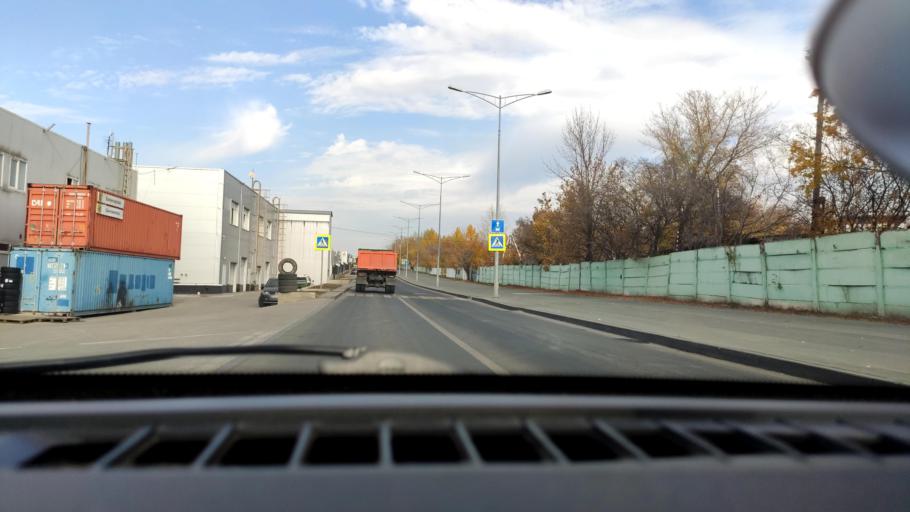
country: RU
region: Samara
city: Petra-Dubrava
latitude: 53.2873
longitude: 50.2848
